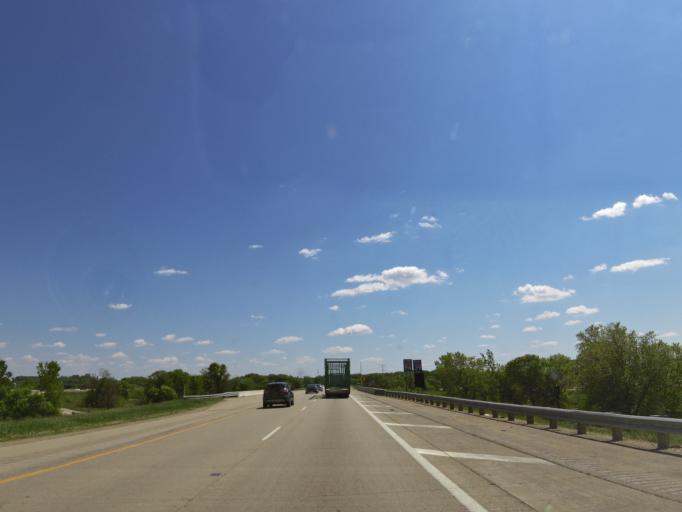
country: US
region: Wisconsin
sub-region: Dane County
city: McFarland
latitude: 43.0502
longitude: -89.2777
